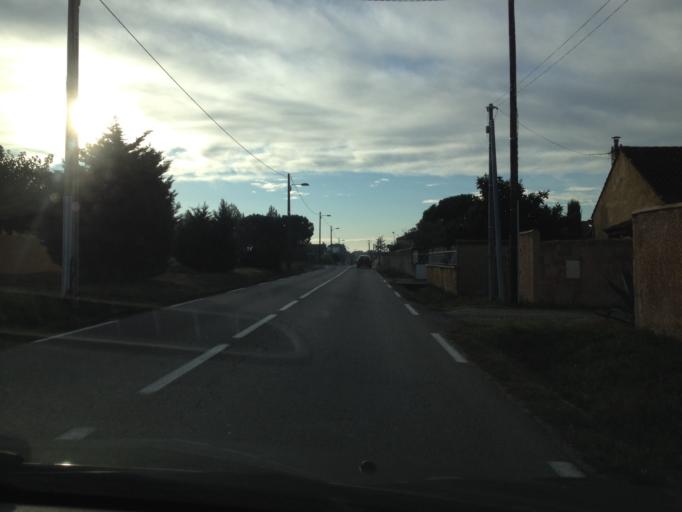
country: FR
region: Provence-Alpes-Cote d'Azur
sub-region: Departement du Vaucluse
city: Sorgues
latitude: 44.0221
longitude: 4.8659
